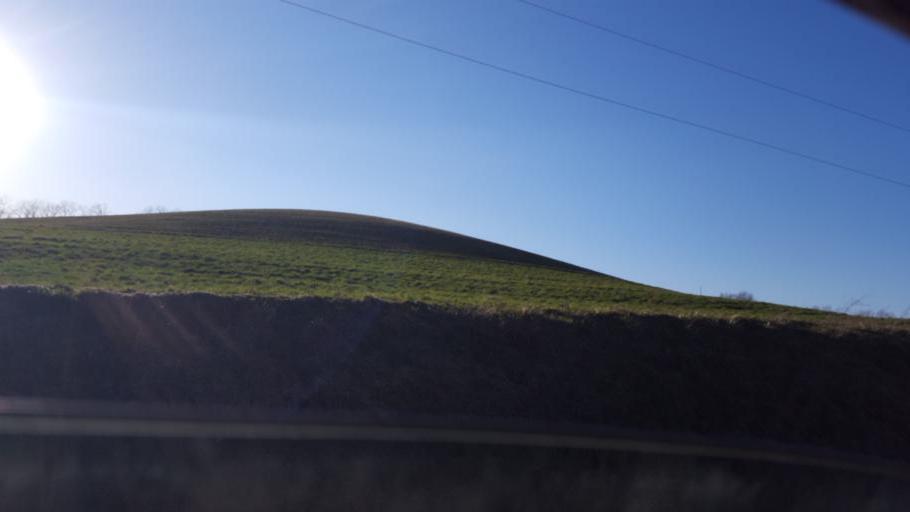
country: US
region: Ohio
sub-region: Wayne County
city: Apple Creek
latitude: 40.6257
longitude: -81.7597
